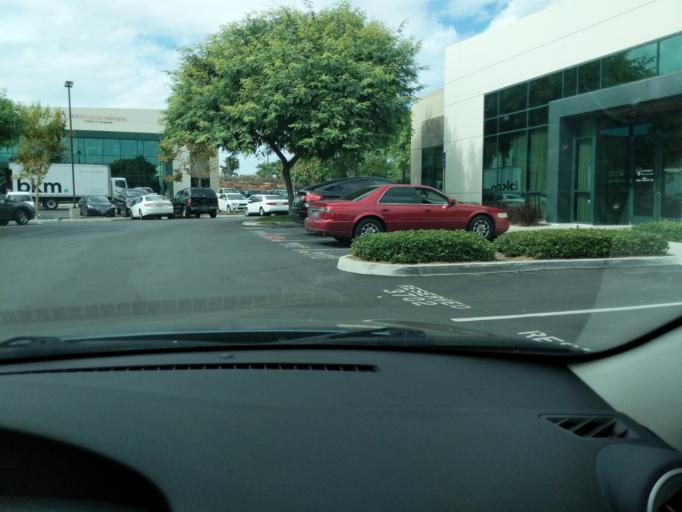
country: US
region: California
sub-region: San Diego County
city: San Diego
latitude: 32.8108
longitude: -117.1213
